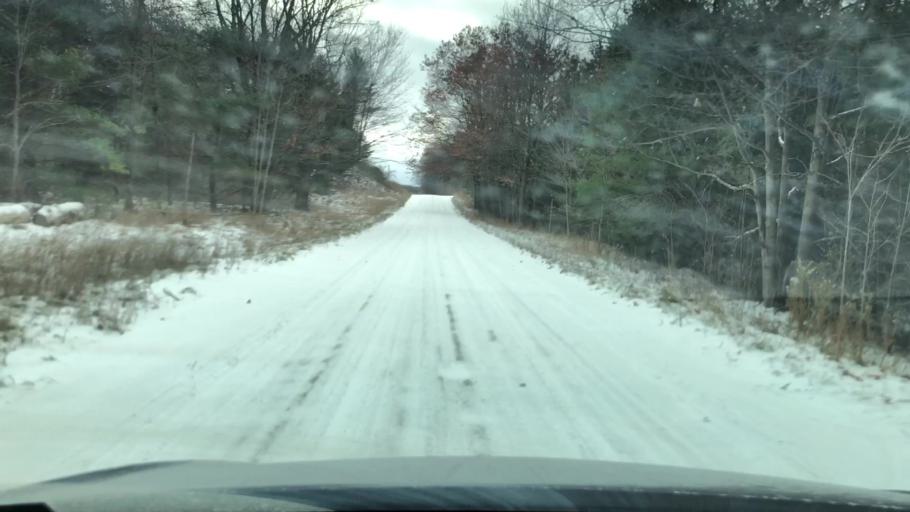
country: US
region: Michigan
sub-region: Antrim County
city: Elk Rapids
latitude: 44.9564
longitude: -85.5155
